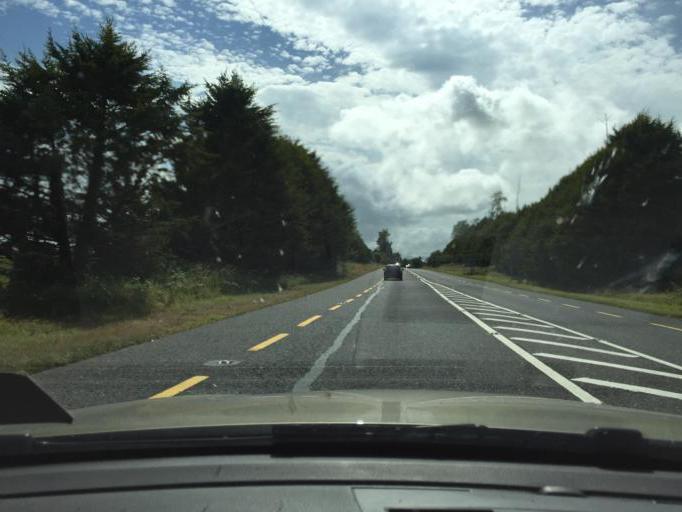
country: IE
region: Munster
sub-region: Waterford
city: Portlaw
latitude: 52.2247
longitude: -7.3451
